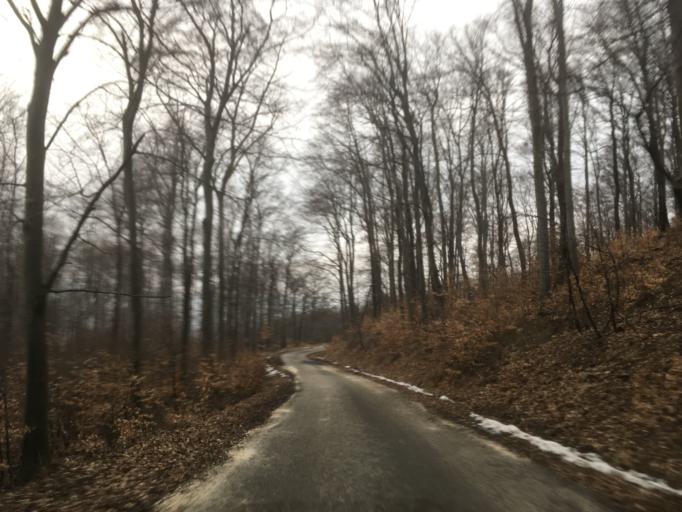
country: HU
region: Pest
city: Pilisszentkereszt
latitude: 47.7223
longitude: 18.8650
